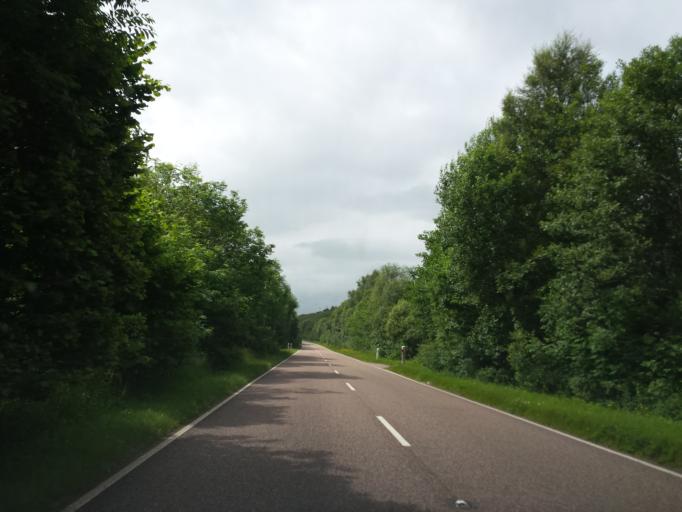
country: GB
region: Scotland
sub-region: Highland
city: Fort William
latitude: 56.8560
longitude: -5.2888
